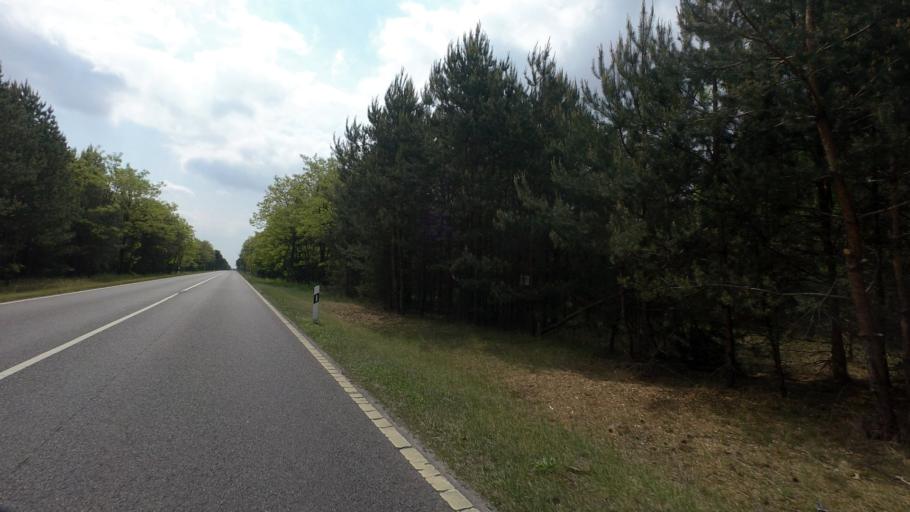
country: DE
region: Brandenburg
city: Lieberose
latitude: 51.9499
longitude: 14.3337
